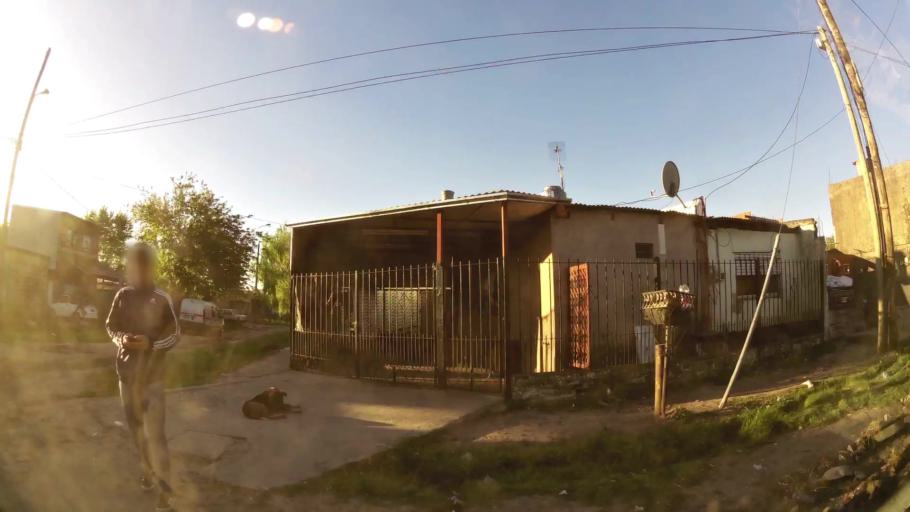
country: AR
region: Buenos Aires
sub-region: Partido de Almirante Brown
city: Adrogue
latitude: -34.7724
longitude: -58.3295
